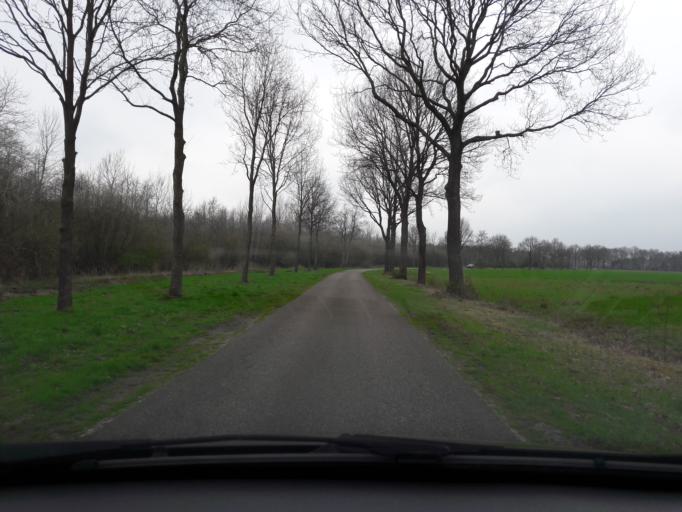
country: NL
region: Drenthe
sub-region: Gemeente Assen
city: Assen
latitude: 52.9320
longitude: 6.6135
